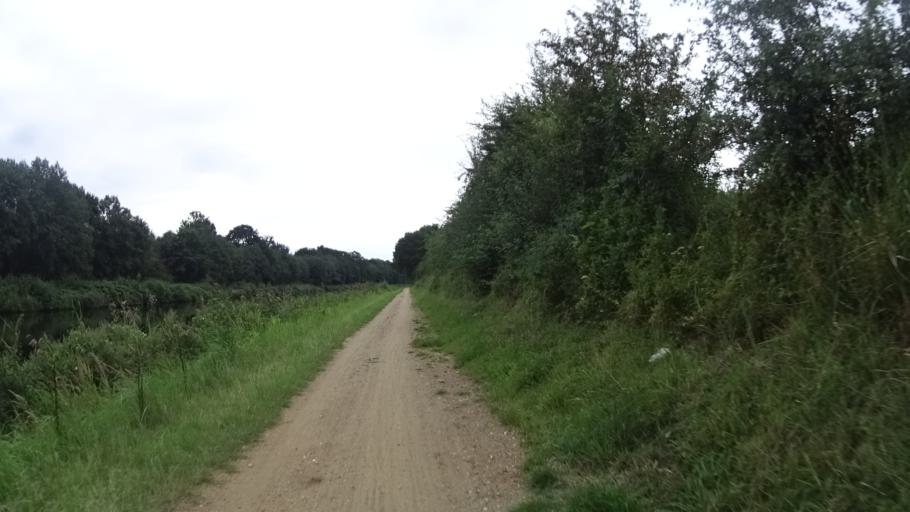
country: DE
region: Schleswig-Holstein
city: Molln
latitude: 53.6184
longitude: 10.6733
